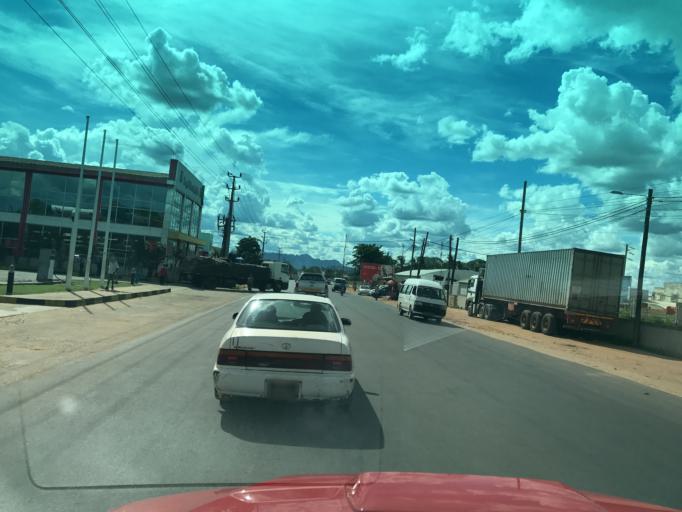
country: MZ
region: Nampula
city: Nampula
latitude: -15.1101
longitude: 39.2503
